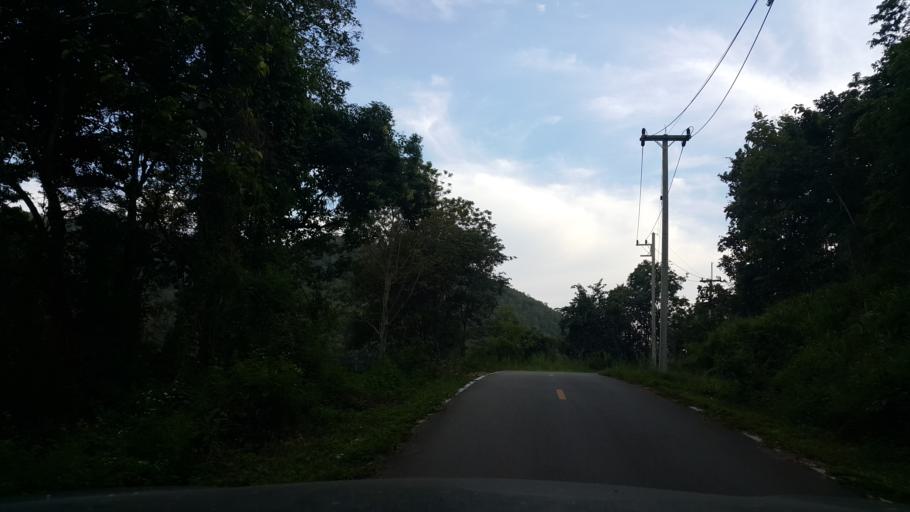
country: TH
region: Chiang Mai
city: San Sai
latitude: 18.9450
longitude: 99.0636
